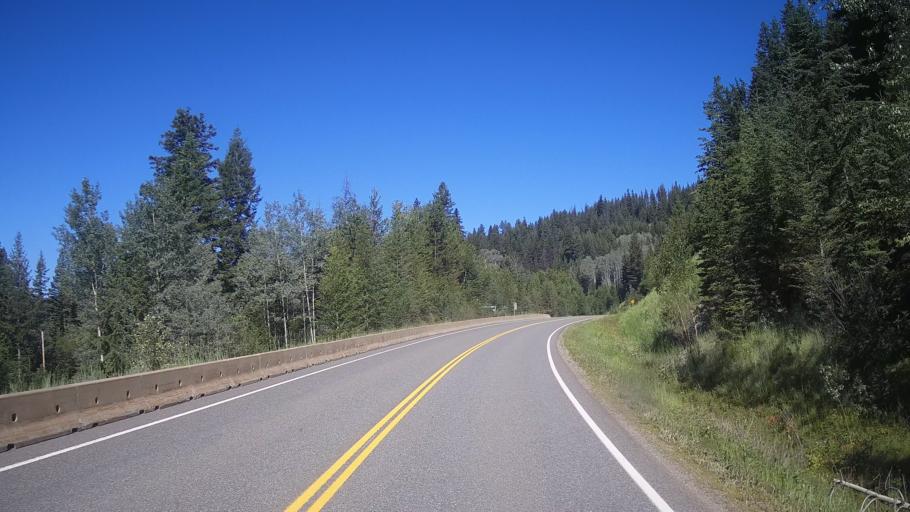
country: CA
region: British Columbia
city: Kamloops
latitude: 51.4714
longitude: -120.5375
